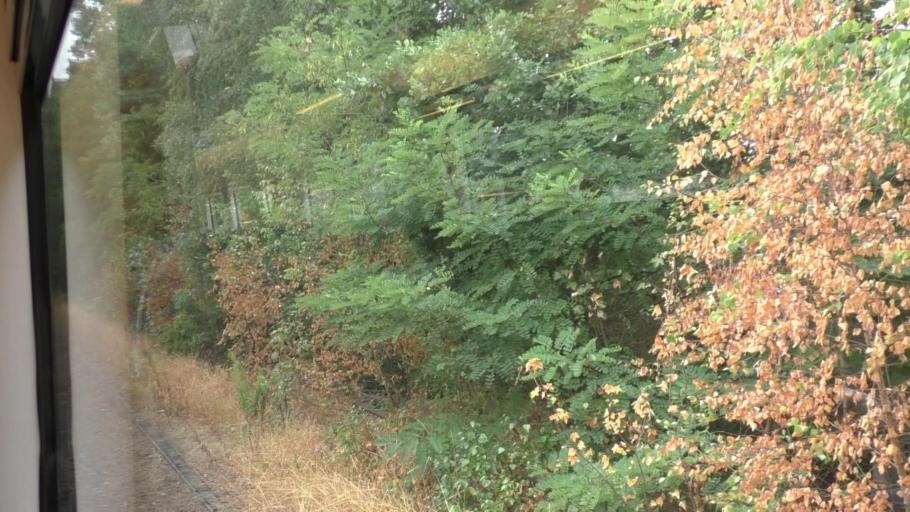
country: DE
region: Saxony
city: Goerlitz
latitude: 51.1290
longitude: 14.9707
